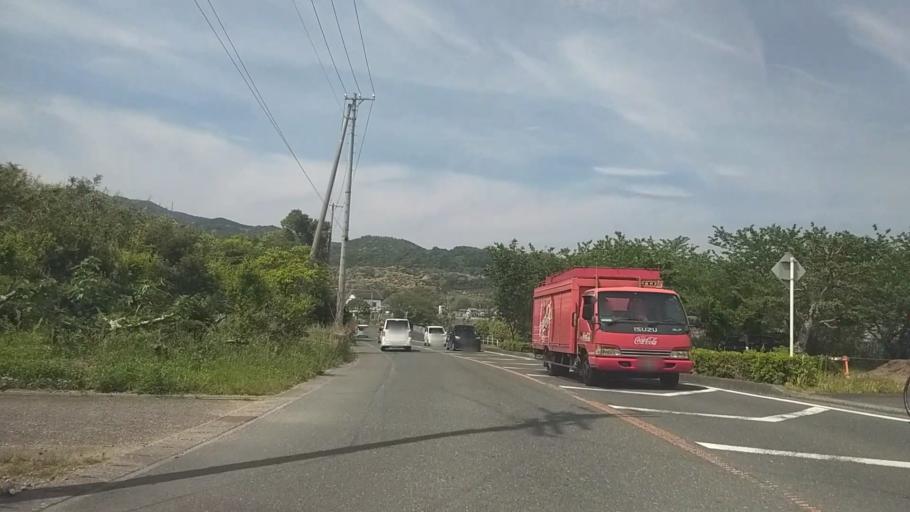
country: JP
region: Shizuoka
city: Kosai-shi
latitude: 34.7950
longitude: 137.6202
